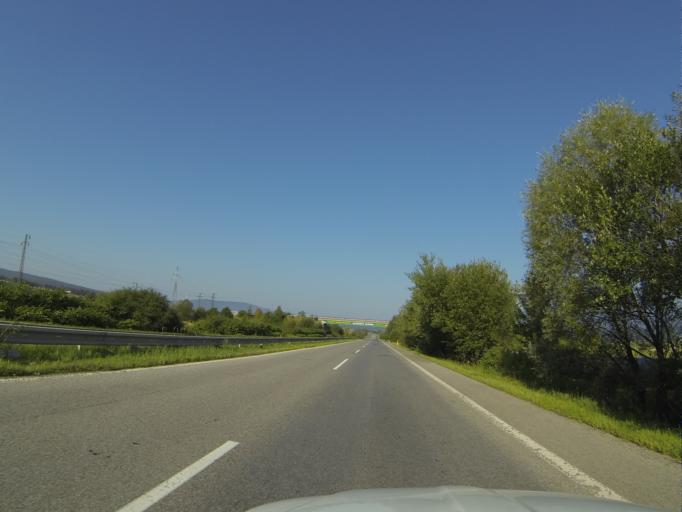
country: SK
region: Nitriansky
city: Bojnice
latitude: 48.7267
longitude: 18.5932
